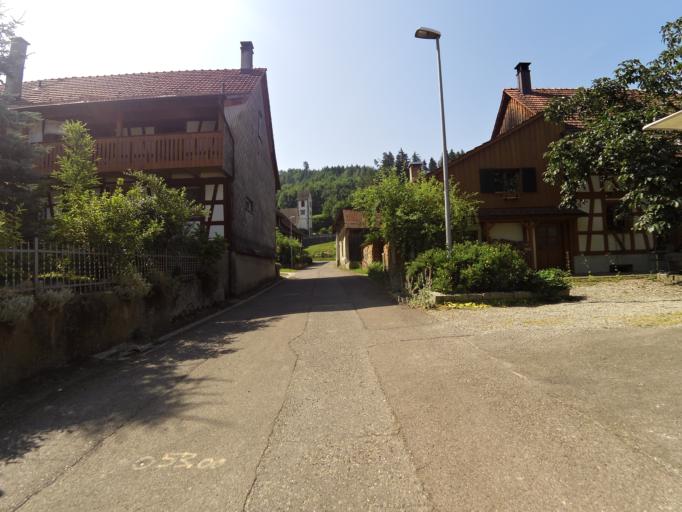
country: CH
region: Thurgau
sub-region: Frauenfeld District
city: Mullheim
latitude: 47.5780
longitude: 8.9809
